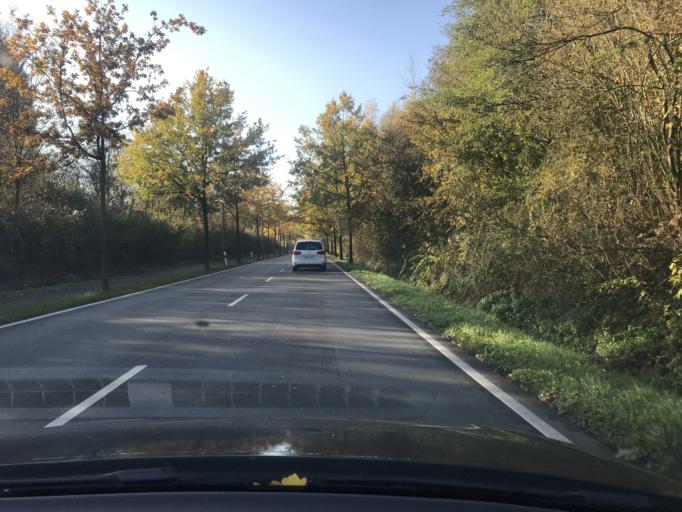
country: DE
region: North Rhine-Westphalia
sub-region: Regierungsbezirk Arnsberg
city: Hamm
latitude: 51.6629
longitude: 7.8544
